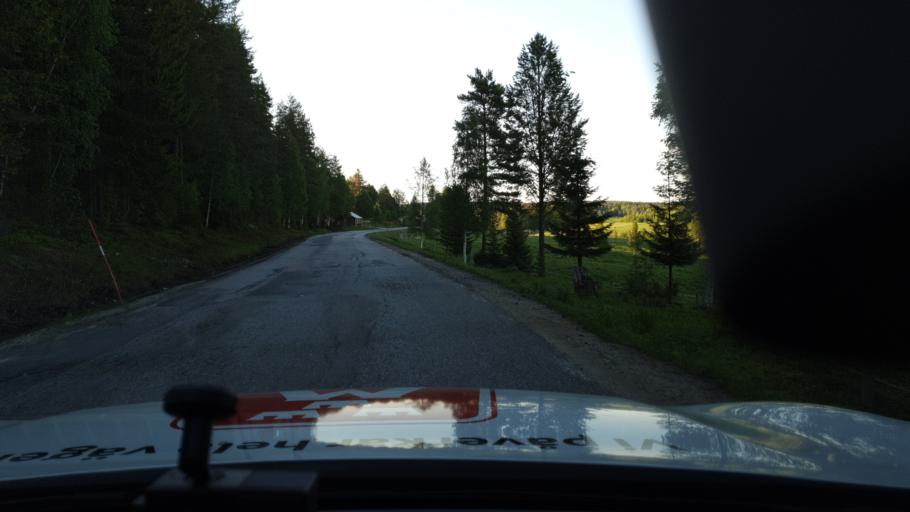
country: SE
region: Vaesterbotten
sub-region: Umea Kommun
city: Roback
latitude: 64.0213
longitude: 20.0863
